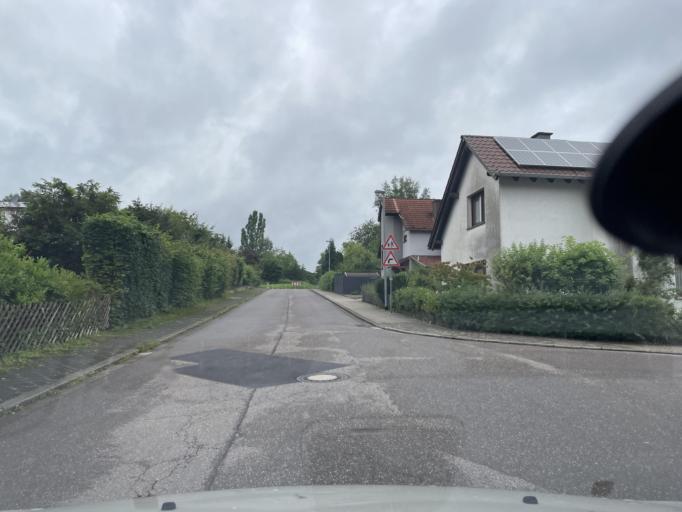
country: DE
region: Saarland
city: Sankt Ingbert
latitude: 49.2666
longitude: 7.1123
